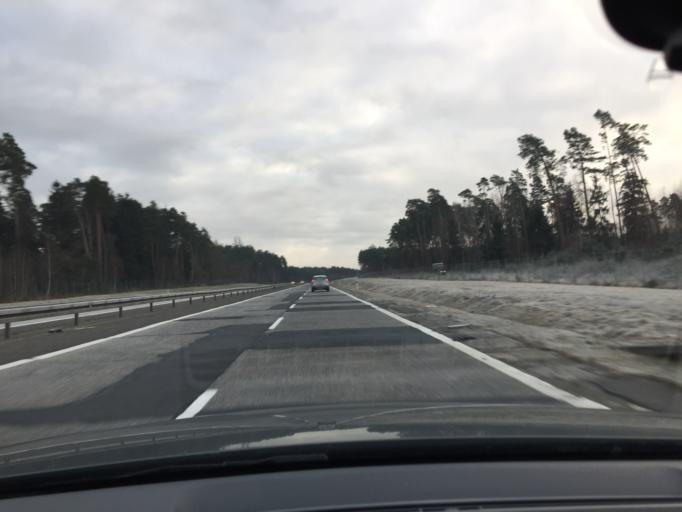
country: PL
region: Lubusz
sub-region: Powiat zarski
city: Lipinki Luzyckie
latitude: 51.5912
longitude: 15.0086
